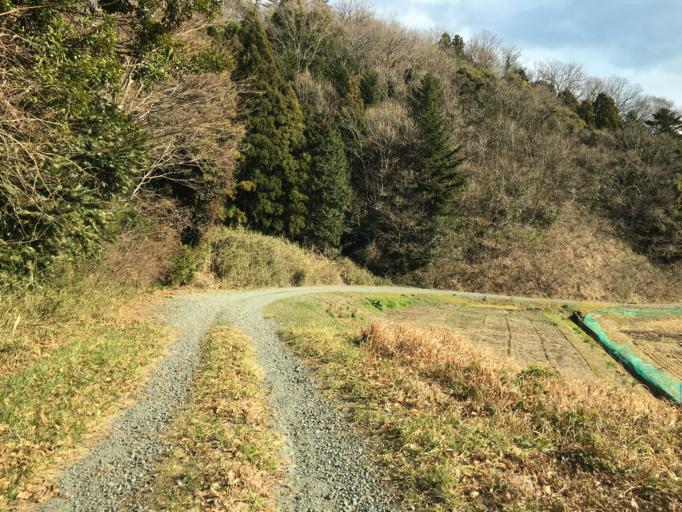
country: JP
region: Fukushima
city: Iwaki
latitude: 37.0953
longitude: 140.9488
